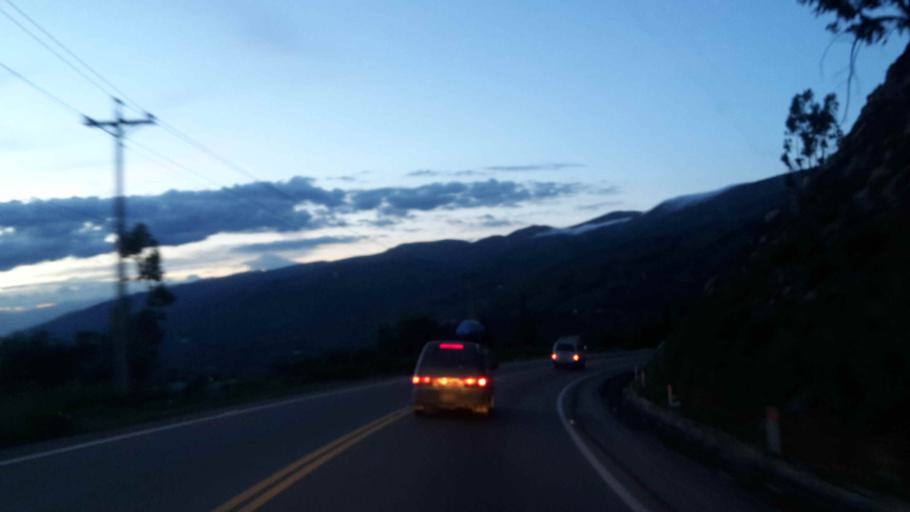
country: BO
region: Cochabamba
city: Colomi
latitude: -17.4215
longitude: -65.9329
